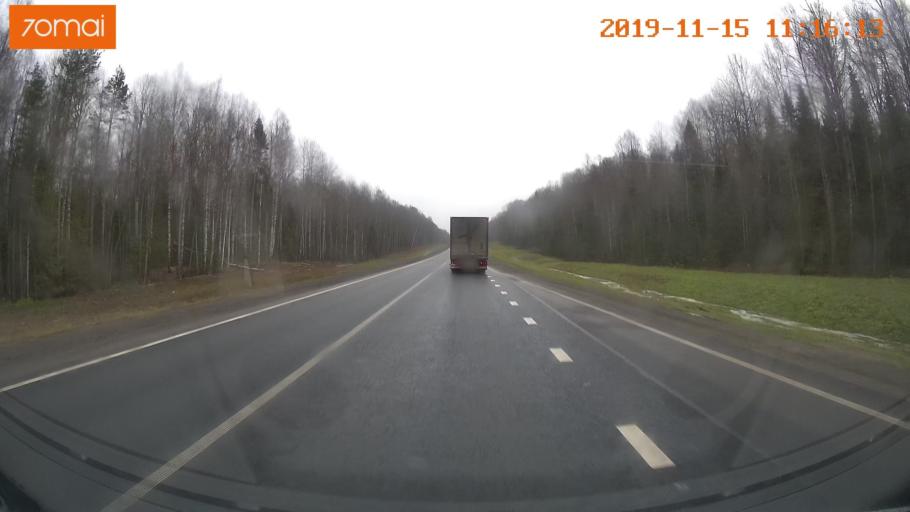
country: RU
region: Vologda
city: Chebsara
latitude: 59.1296
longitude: 39.2252
